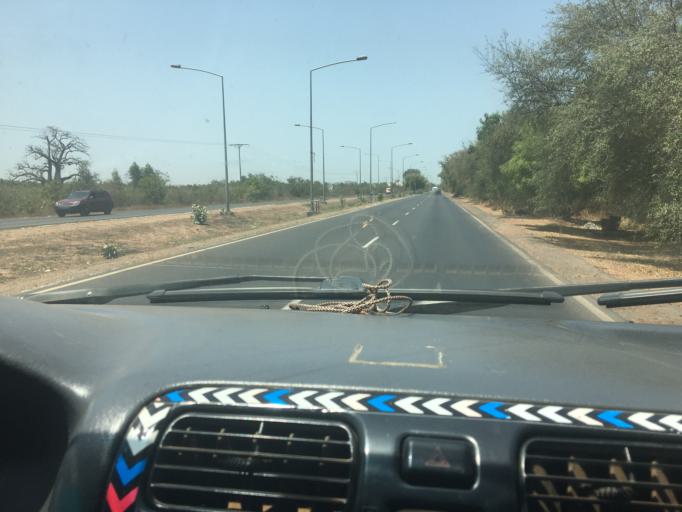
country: GM
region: Banjul
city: Bakau
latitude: 13.4688
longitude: -16.6428
